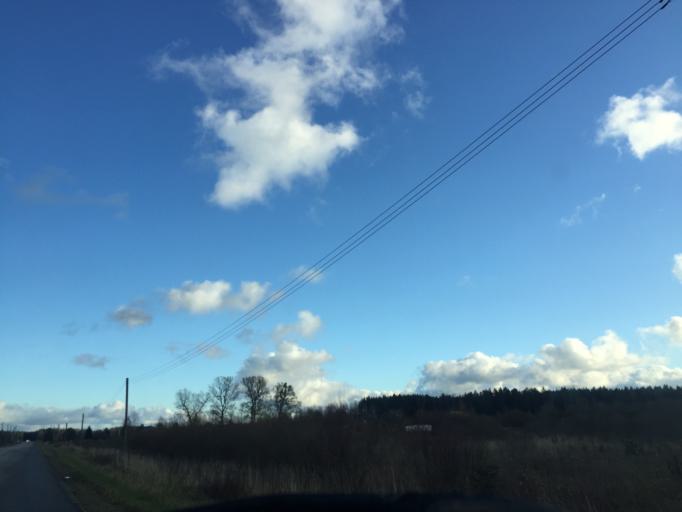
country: LV
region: Incukalns
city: Incukalns
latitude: 57.0939
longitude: 24.7081
